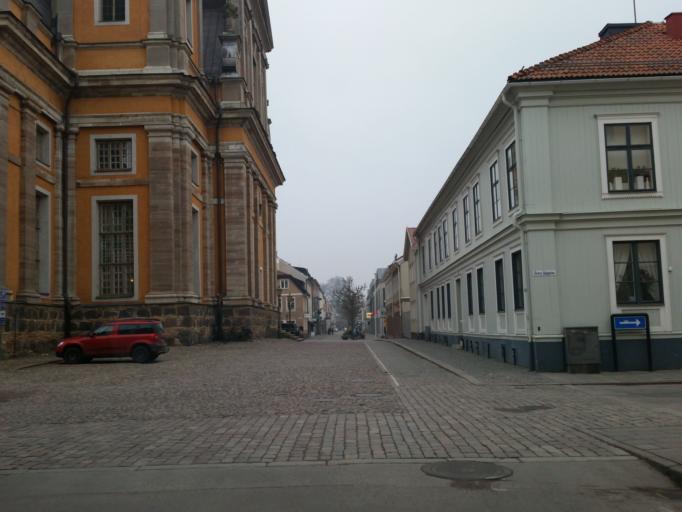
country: SE
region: Kalmar
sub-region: Kalmar Kommun
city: Kalmar
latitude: 56.6649
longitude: 16.3660
